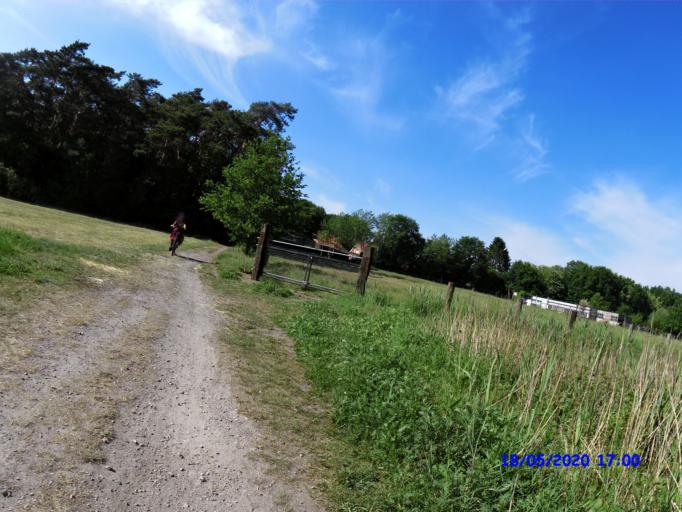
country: BE
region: Flanders
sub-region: Provincie Antwerpen
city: Herentals
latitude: 51.1793
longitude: 4.8222
